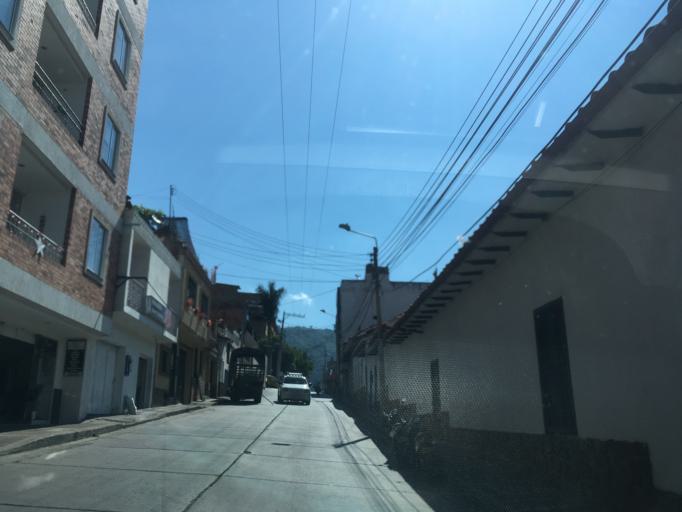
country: CO
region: Santander
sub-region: San Gil
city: San Gil
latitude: 6.5580
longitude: -73.1331
